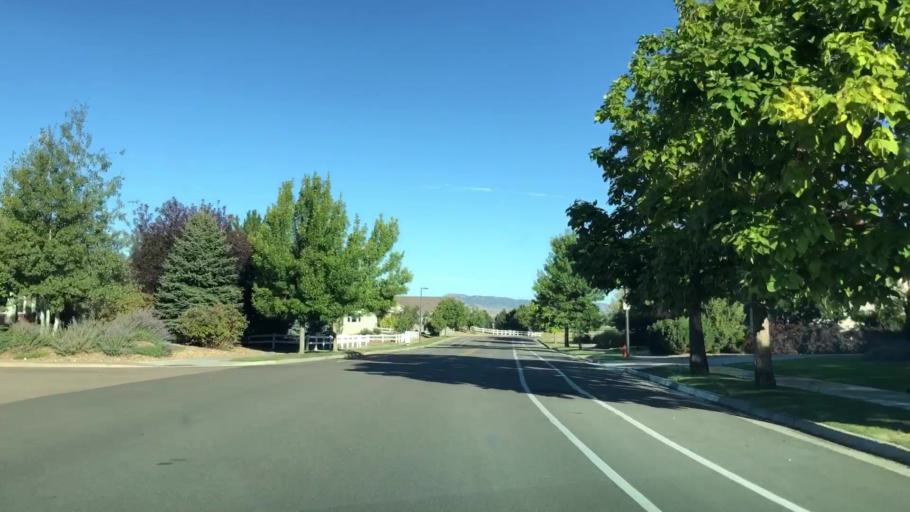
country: US
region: Colorado
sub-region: Larimer County
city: Loveland
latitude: 40.4614
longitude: -105.0348
